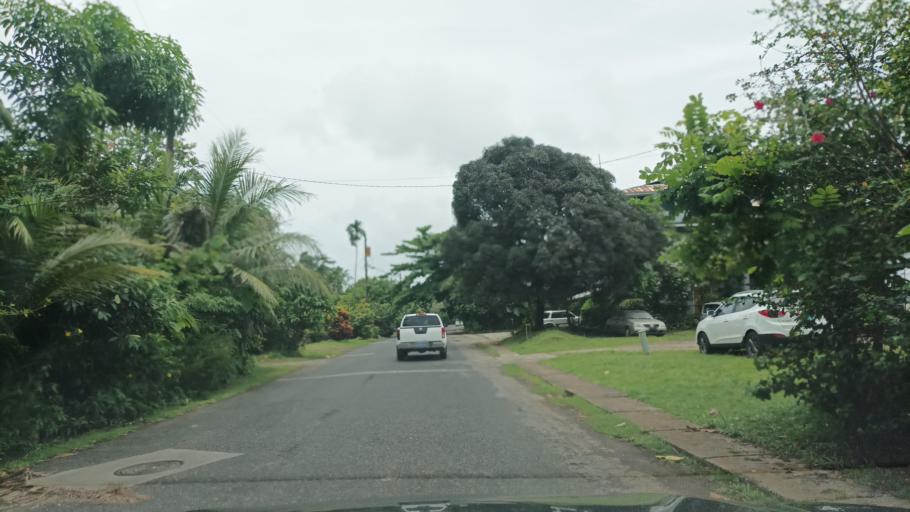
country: FM
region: Pohnpei
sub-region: Kolonia Municipality
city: Kolonia
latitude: 6.9589
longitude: 158.2086
